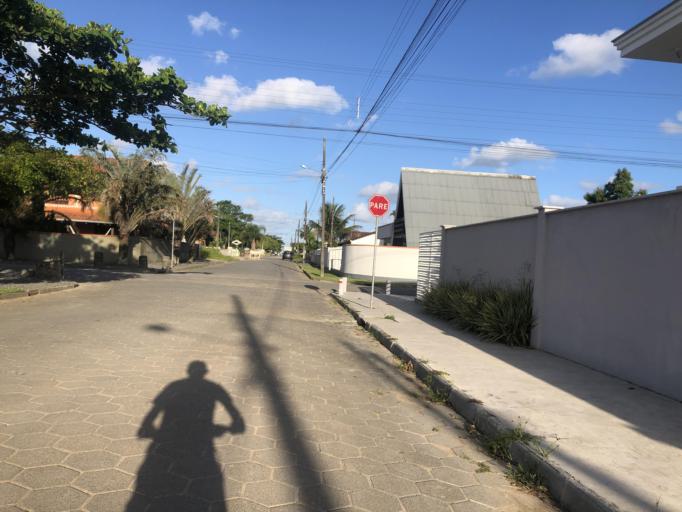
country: BR
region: Santa Catarina
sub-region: Sao Francisco Do Sul
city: Sao Francisco do Sul
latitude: -26.2173
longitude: -48.5303
